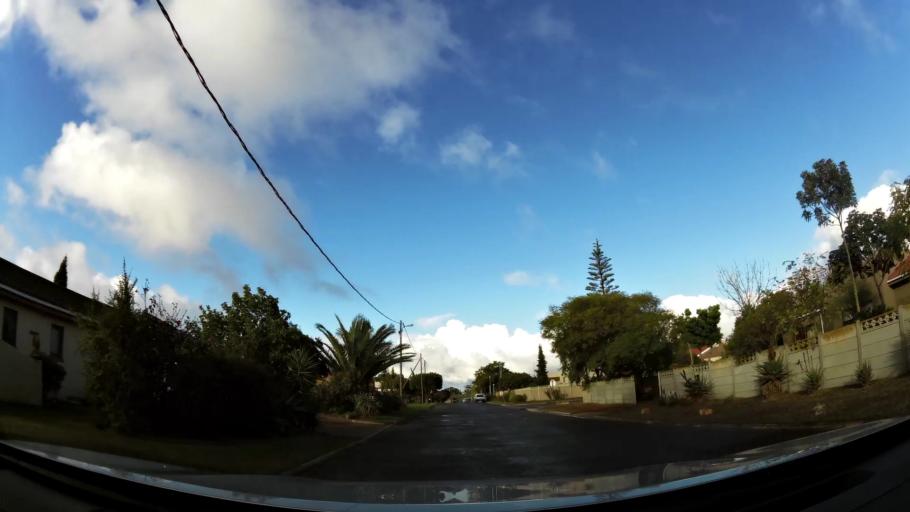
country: ZA
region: Western Cape
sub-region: Eden District Municipality
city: Riversdale
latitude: -34.2084
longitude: 21.5819
